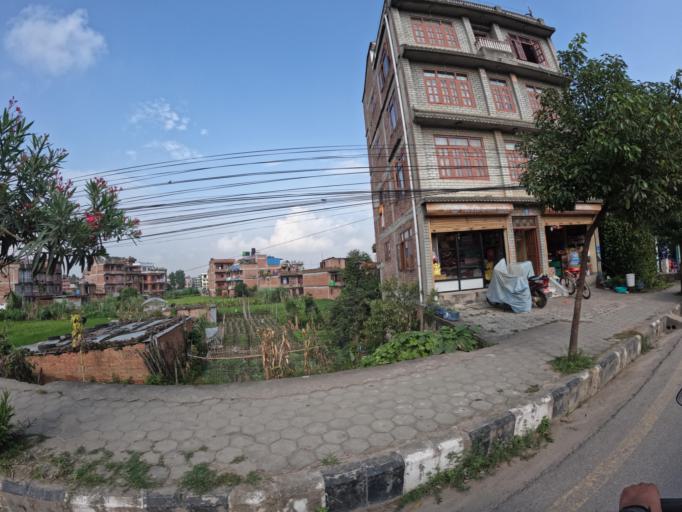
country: NP
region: Central Region
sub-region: Bagmati Zone
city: Bhaktapur
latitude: 27.6772
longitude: 85.4297
